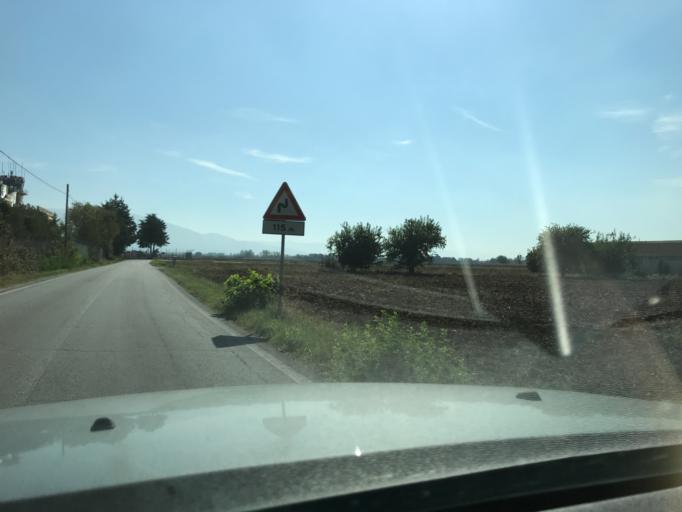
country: IT
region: Umbria
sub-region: Provincia di Perugia
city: Ospedalicchio
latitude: 43.0932
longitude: 12.5014
